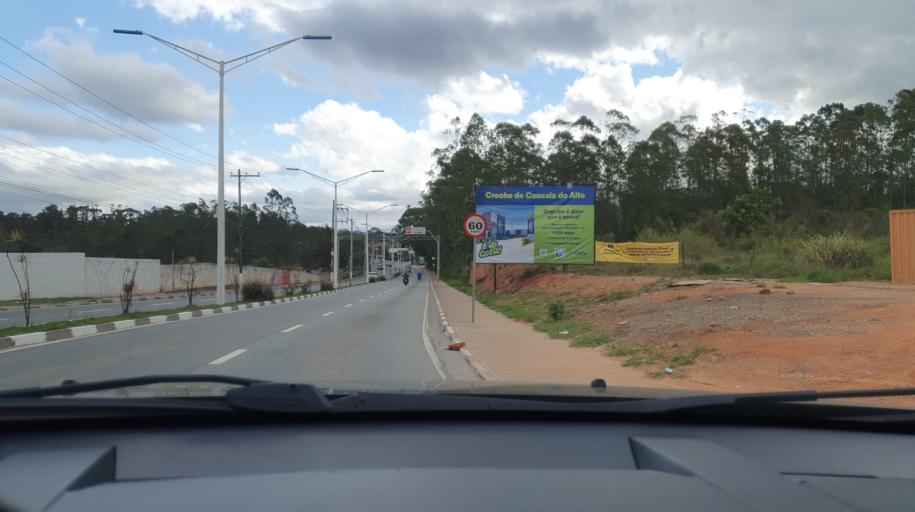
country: BR
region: Sao Paulo
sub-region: Cotia
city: Cotia
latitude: -23.6165
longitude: -46.9721
